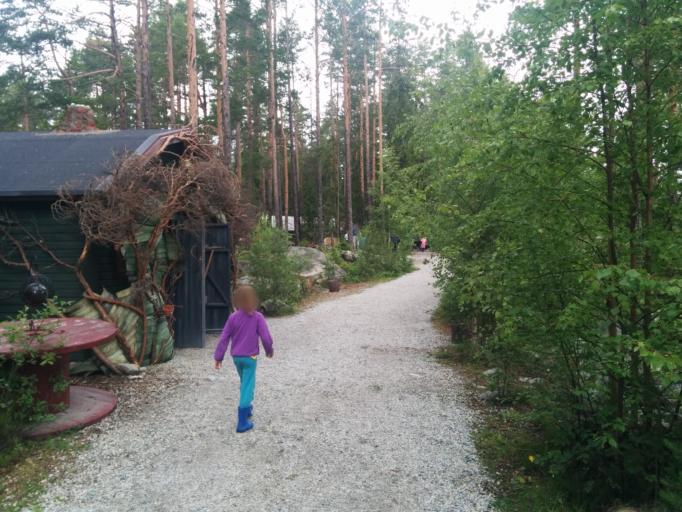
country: SE
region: Gaevleborg
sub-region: Nordanstigs Kommun
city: Bergsjoe
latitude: 61.9565
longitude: 17.3228
